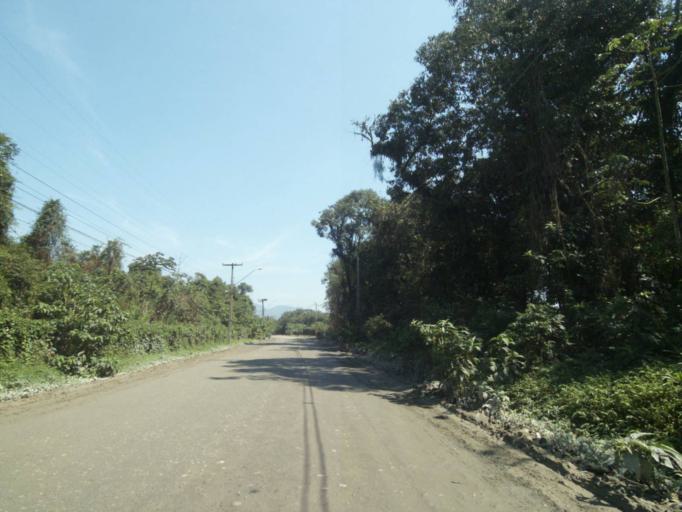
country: BR
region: Parana
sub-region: Paranagua
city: Paranagua
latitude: -25.5465
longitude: -48.5731
